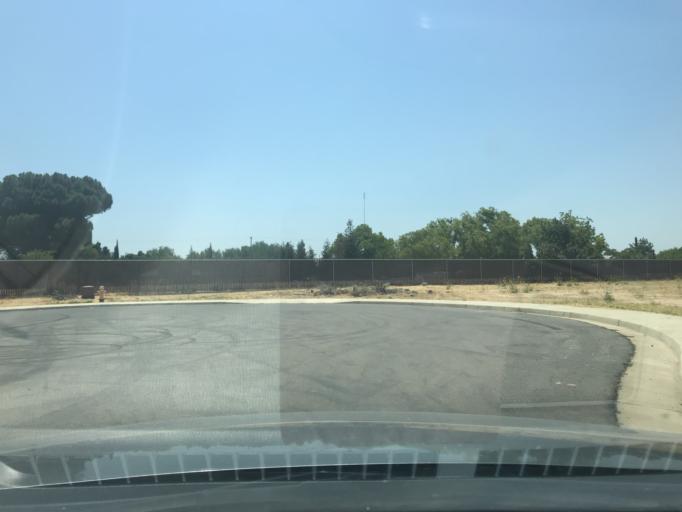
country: US
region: California
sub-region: Merced County
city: Winton
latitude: 37.3726
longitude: -120.6006
